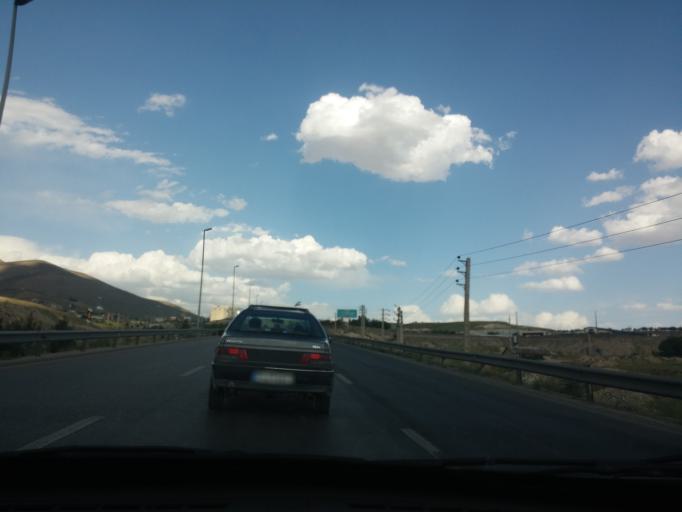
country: IR
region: Tehran
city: Damavand
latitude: 35.7176
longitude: 51.9291
